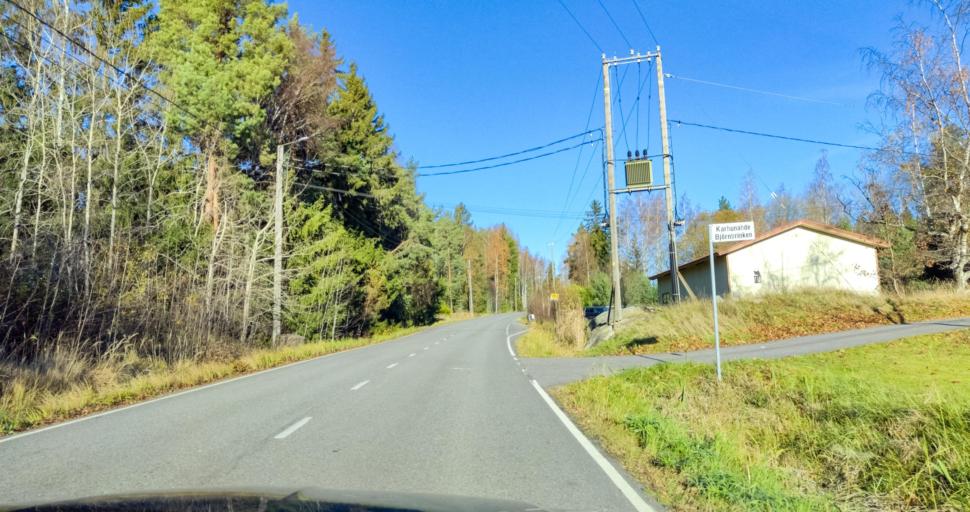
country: FI
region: Varsinais-Suomi
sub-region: Turku
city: Turku
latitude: 60.3983
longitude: 22.2061
